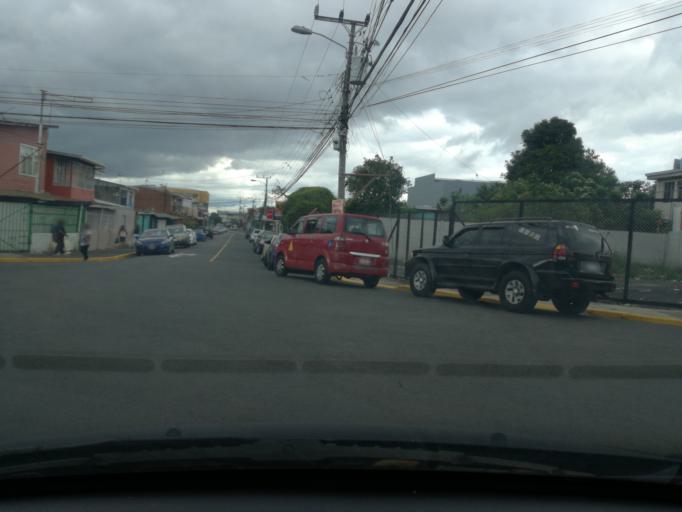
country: CR
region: San Jose
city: San Pedro
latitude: 9.9186
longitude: -84.0517
